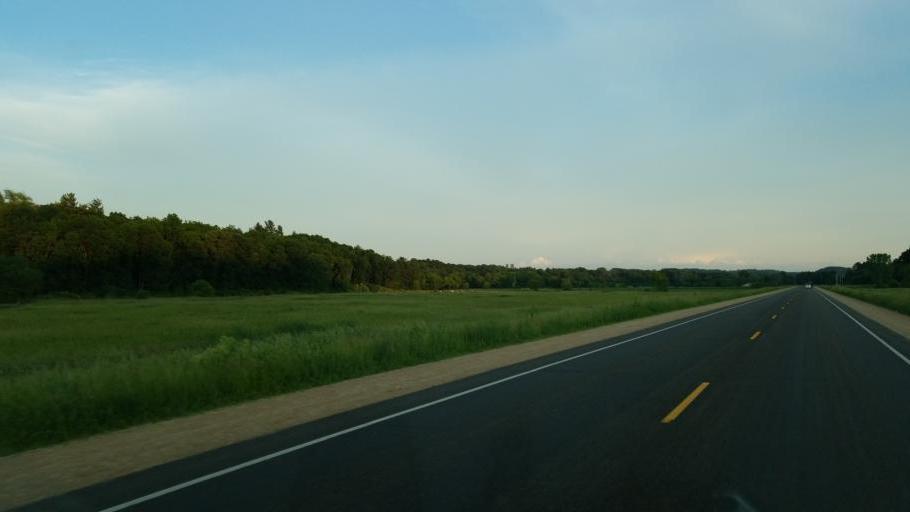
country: US
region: Wisconsin
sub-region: Monroe County
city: Tomah
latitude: 43.9457
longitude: -90.5037
